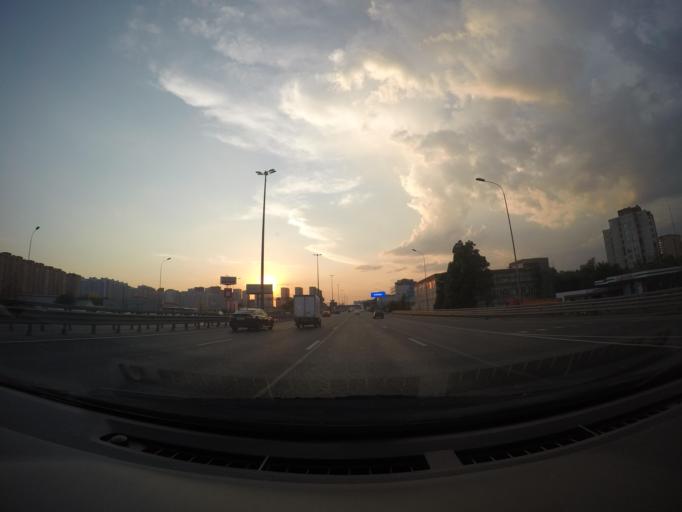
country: RU
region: Moskovskaya
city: Lyubertsy
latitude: 55.6674
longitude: 37.8754
